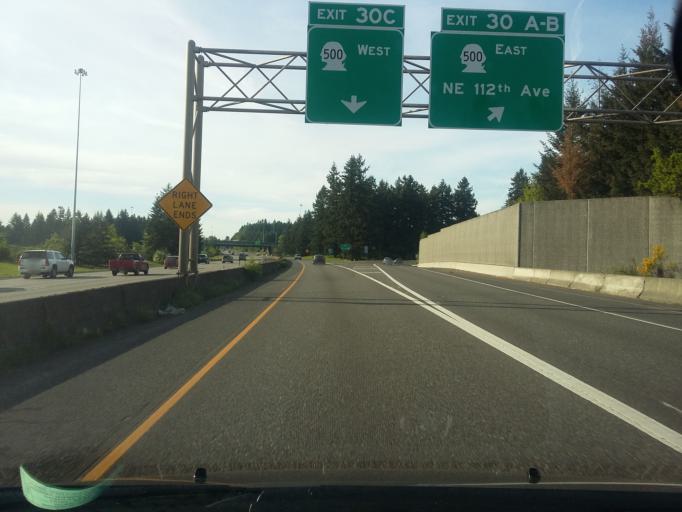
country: US
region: Washington
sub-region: Clark County
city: Orchards
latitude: 45.6532
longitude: -122.5674
